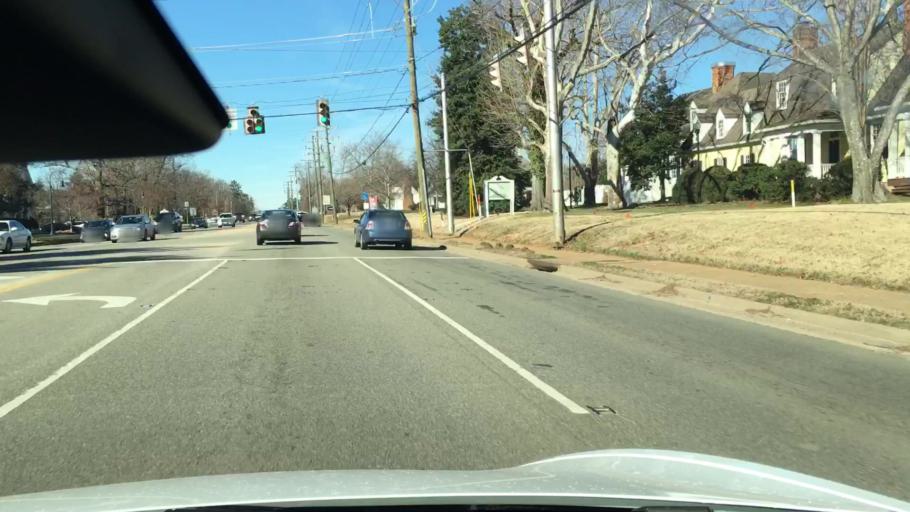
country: US
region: Virginia
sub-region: Chesterfield County
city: Brandermill
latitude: 37.5036
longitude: -77.6514
